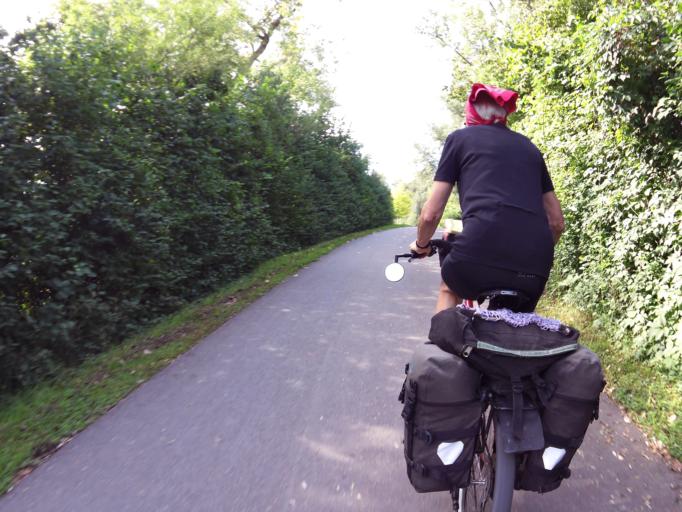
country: DE
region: Baden-Wuerttemberg
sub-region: Regierungsbezirk Stuttgart
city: Nurtingen
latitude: 48.6271
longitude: 9.3326
